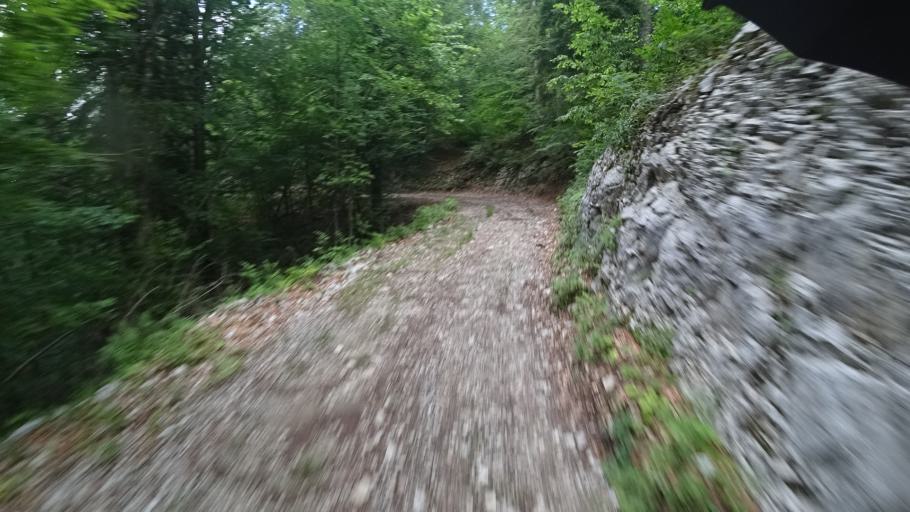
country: SI
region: Osilnica
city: Osilnica
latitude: 45.4930
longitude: 14.6749
